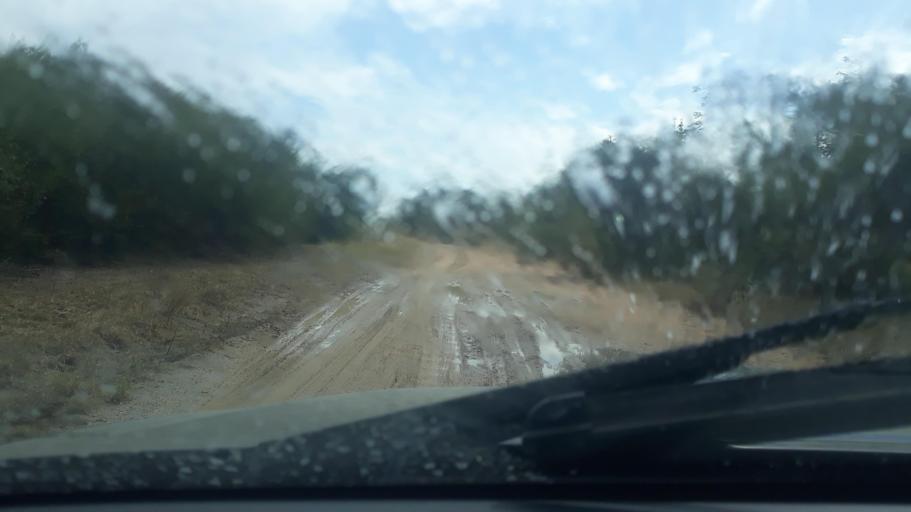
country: BR
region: Bahia
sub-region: Riacho De Santana
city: Riacho de Santana
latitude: -13.8769
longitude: -43.0207
